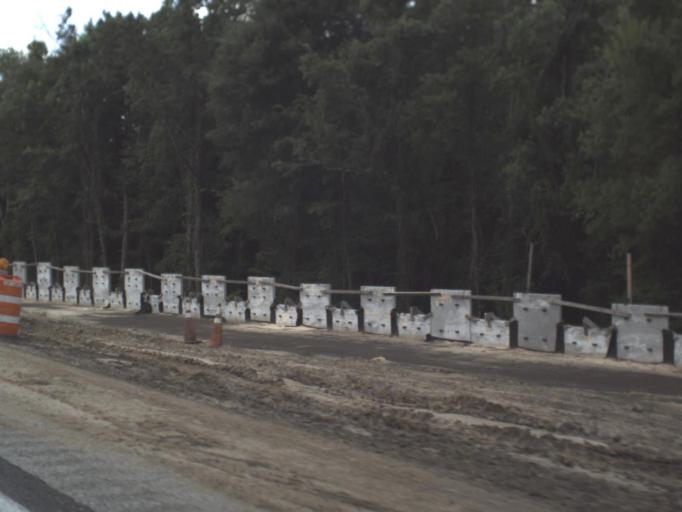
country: US
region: Florida
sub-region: Alachua County
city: High Springs
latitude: 29.7935
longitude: -82.5152
